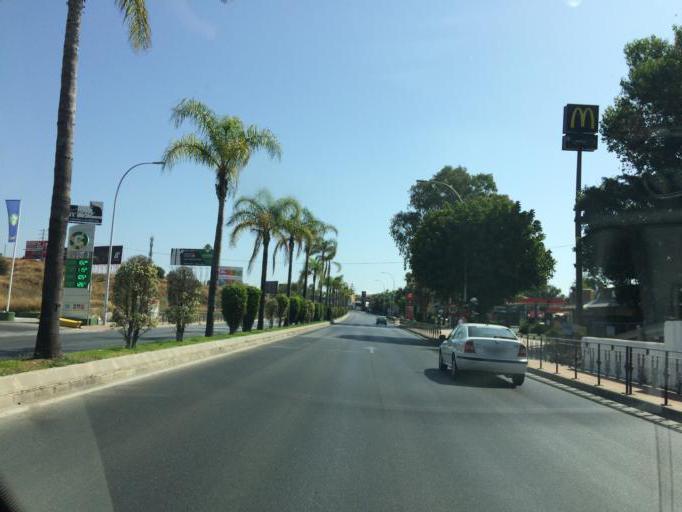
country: ES
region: Andalusia
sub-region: Provincia de Malaga
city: Torremolinos
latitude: 36.6427
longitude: -4.4926
